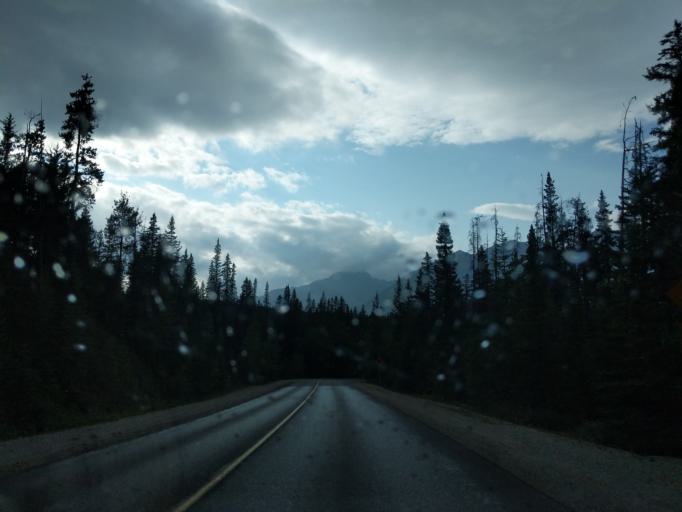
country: CA
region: Alberta
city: Banff
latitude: 51.1642
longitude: -115.5770
